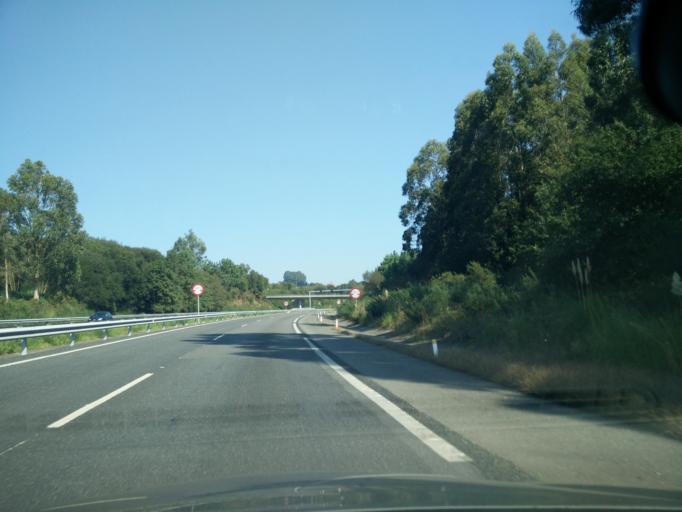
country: ES
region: Galicia
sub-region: Provincia da Coruna
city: Mino
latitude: 43.3896
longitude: -8.1773
